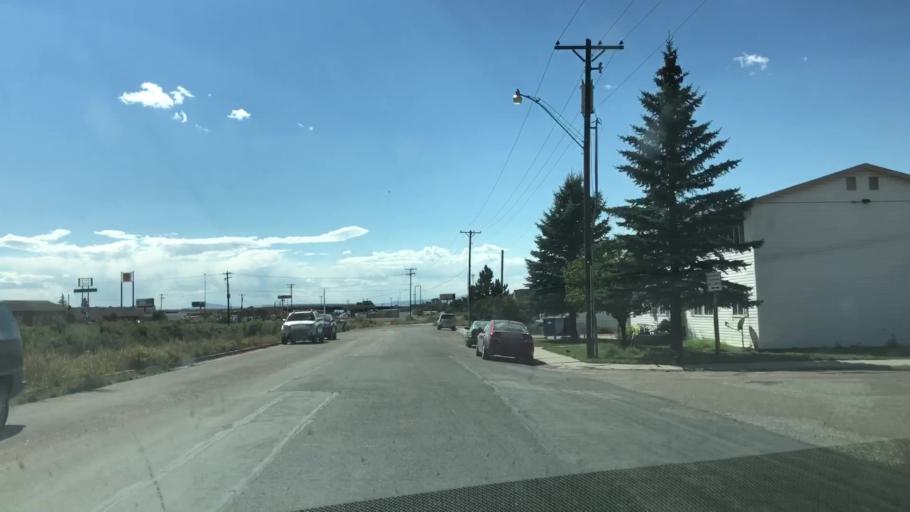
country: US
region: Wyoming
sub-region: Albany County
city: Laramie
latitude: 41.3015
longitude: -105.5905
